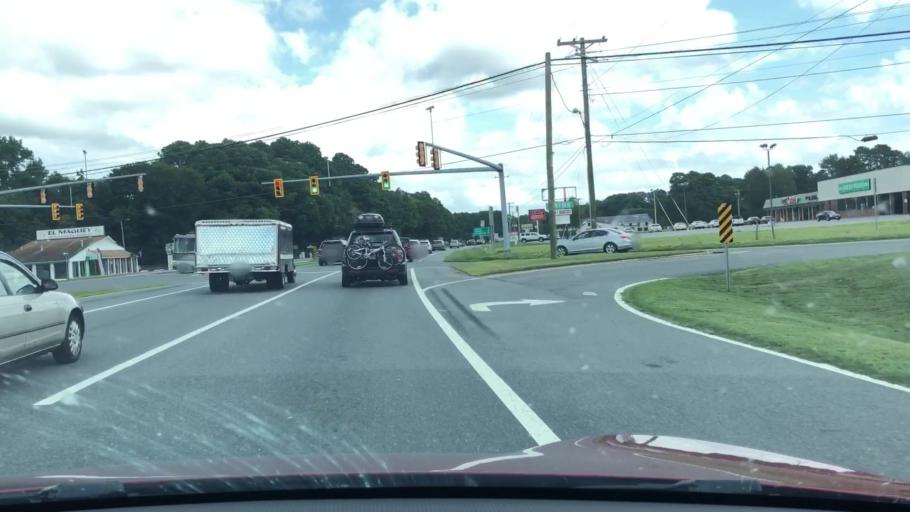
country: US
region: Virginia
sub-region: Northampton County
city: Exmore
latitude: 37.5398
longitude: -75.8235
